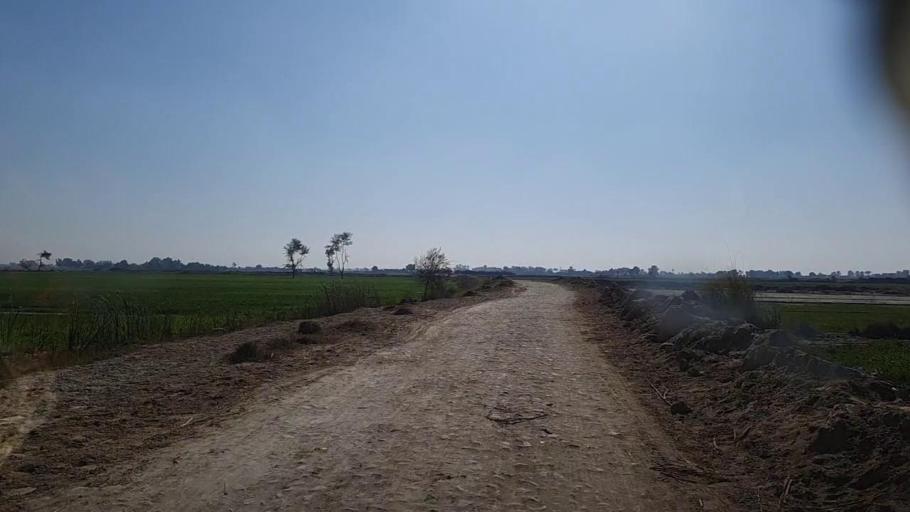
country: PK
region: Sindh
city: Khairpur
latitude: 28.0371
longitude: 69.7828
